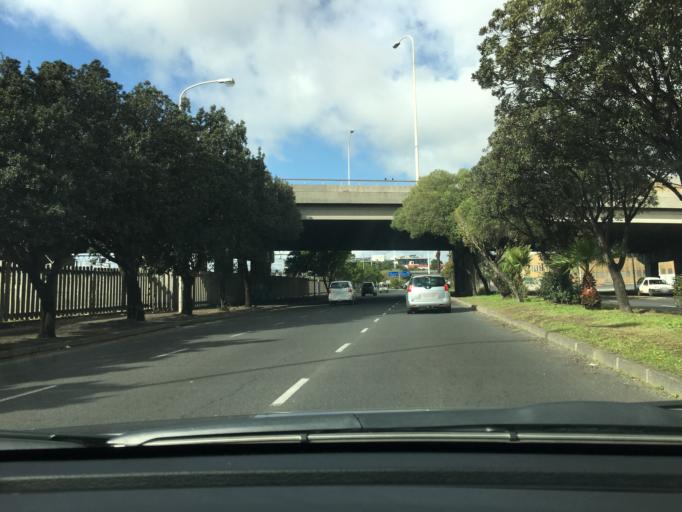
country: ZA
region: Western Cape
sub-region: City of Cape Town
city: Cape Town
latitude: -33.9254
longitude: 18.4297
